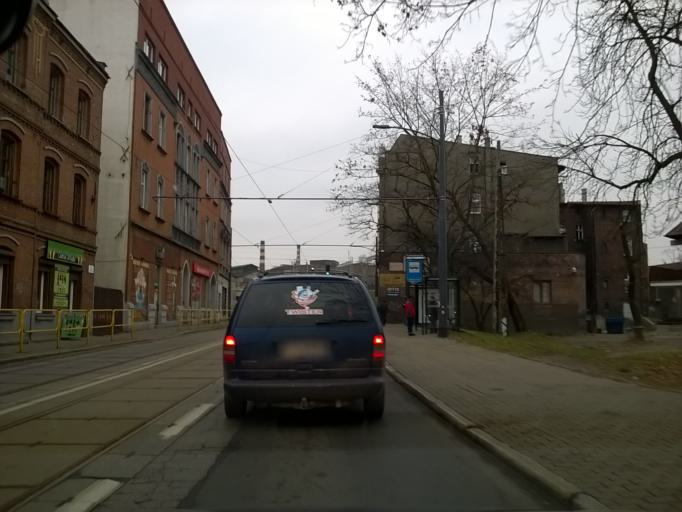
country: PL
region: Silesian Voivodeship
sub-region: Swietochlowice
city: Swietochlowice
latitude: 50.2801
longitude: 18.9448
